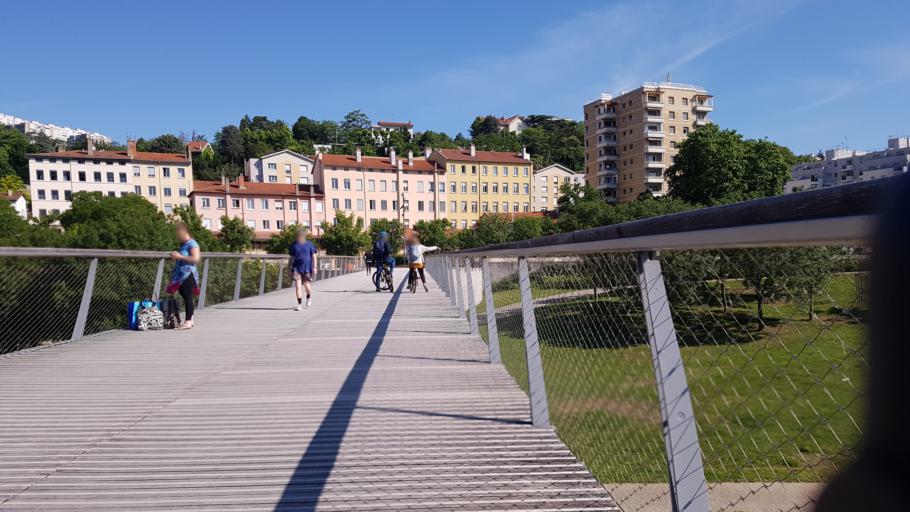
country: FR
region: Rhone-Alpes
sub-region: Departement du Rhone
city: Caluire-et-Cuire
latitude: 45.7874
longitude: 4.8545
